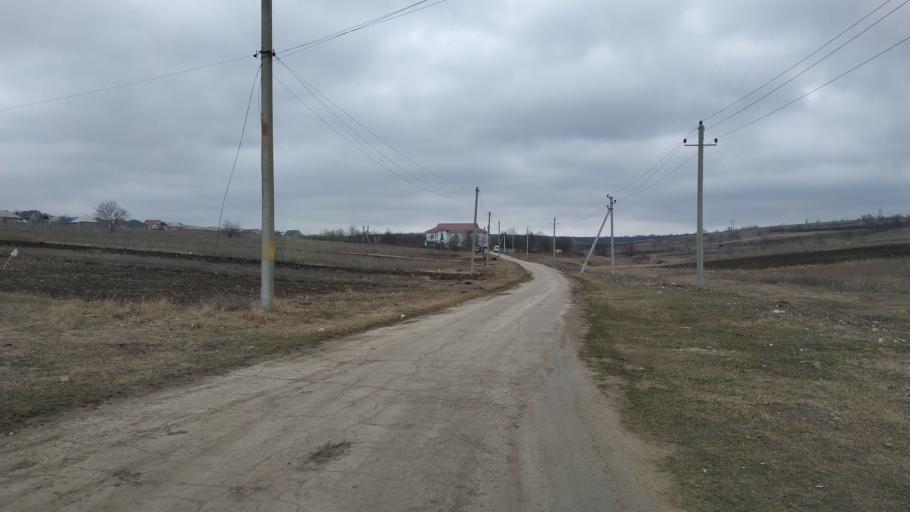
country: MD
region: Laloveni
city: Ialoveni
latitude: 46.9409
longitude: 28.7936
